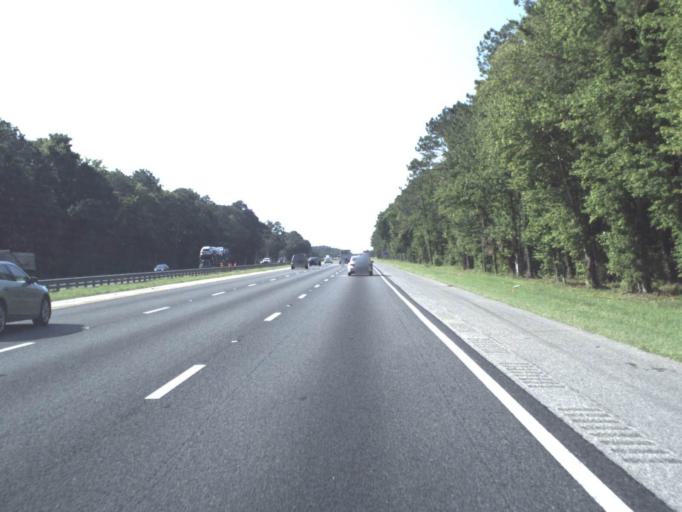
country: US
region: Florida
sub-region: Saint Johns County
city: Villano Beach
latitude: 30.0014
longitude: -81.4713
